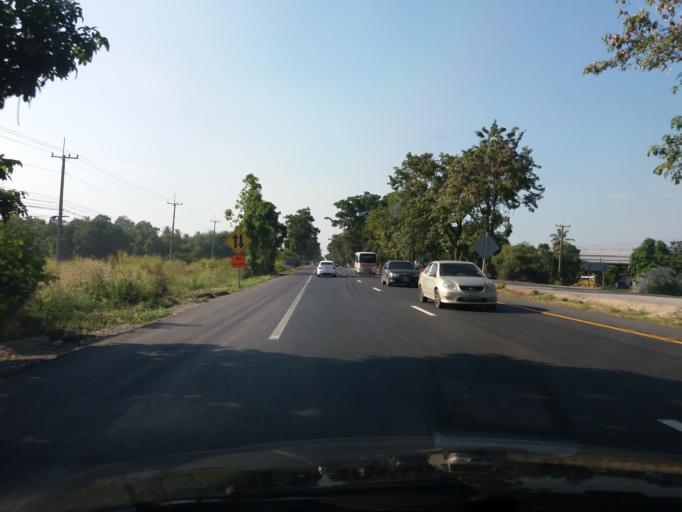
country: TH
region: Nakhon Sawan
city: Kao Liao
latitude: 15.7733
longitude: 99.9822
